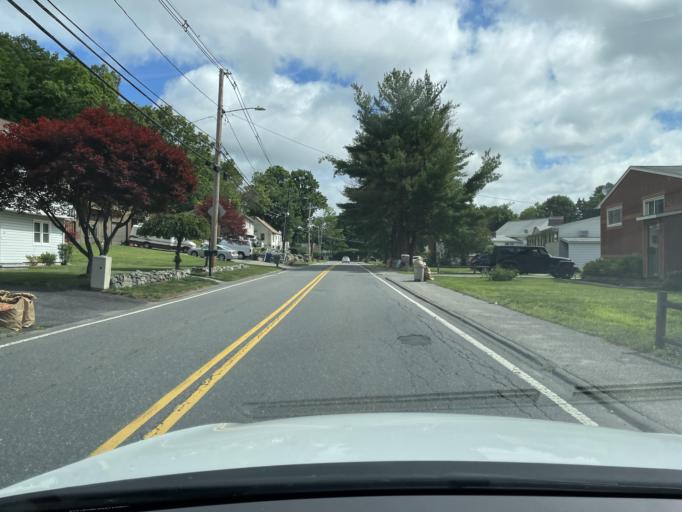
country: US
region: Massachusetts
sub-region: Middlesex County
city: Woburn
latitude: 42.4879
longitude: -71.1762
